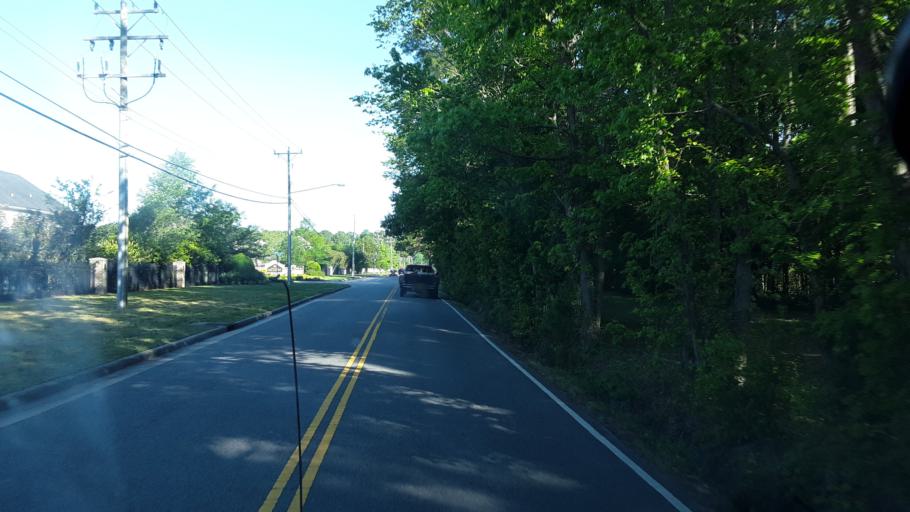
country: US
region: Virginia
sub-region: City of Chesapeake
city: Chesapeake
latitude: 36.7554
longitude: -76.1322
